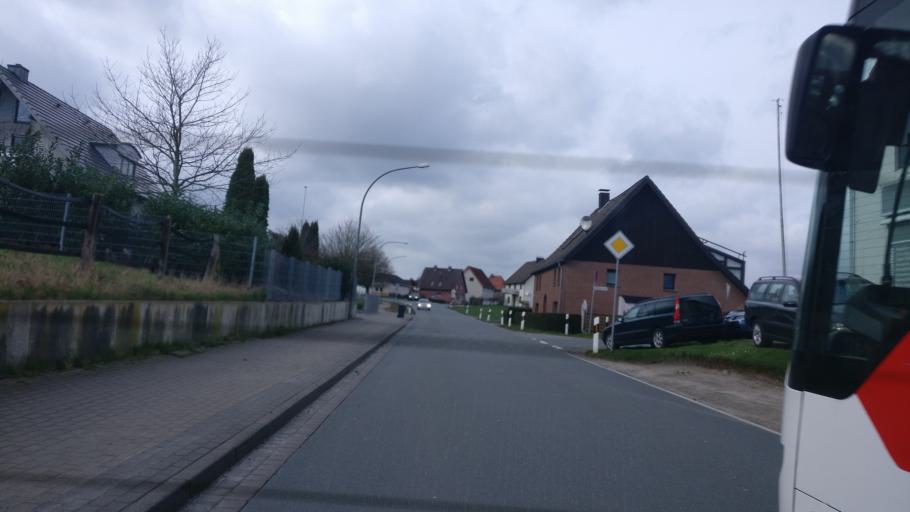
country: DE
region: North Rhine-Westphalia
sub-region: Regierungsbezirk Detmold
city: Lage
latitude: 52.0166
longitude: 8.7894
